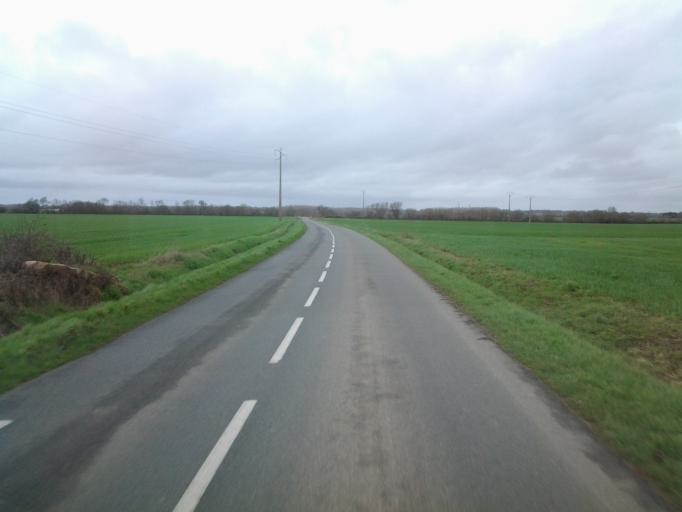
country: FR
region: Pays de la Loire
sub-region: Departement de la Vendee
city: Longeville-sur-Mer
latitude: 46.4342
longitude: -1.4865
